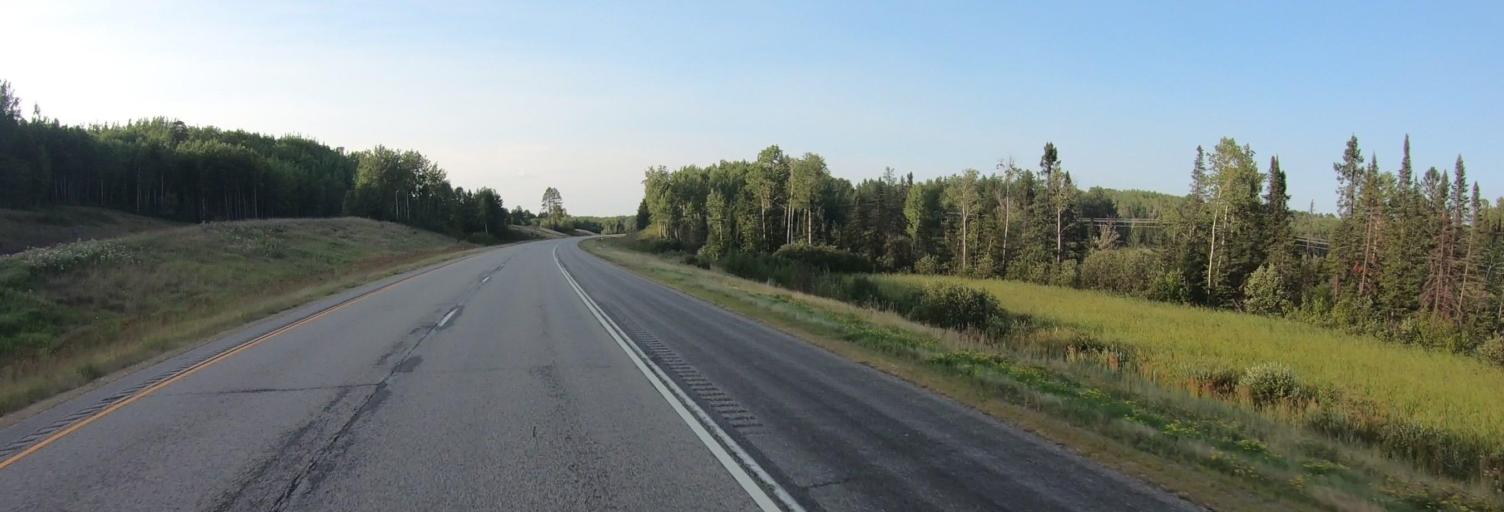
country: US
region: Minnesota
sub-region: Saint Louis County
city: Mountain Iron
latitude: 47.6819
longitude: -92.6381
